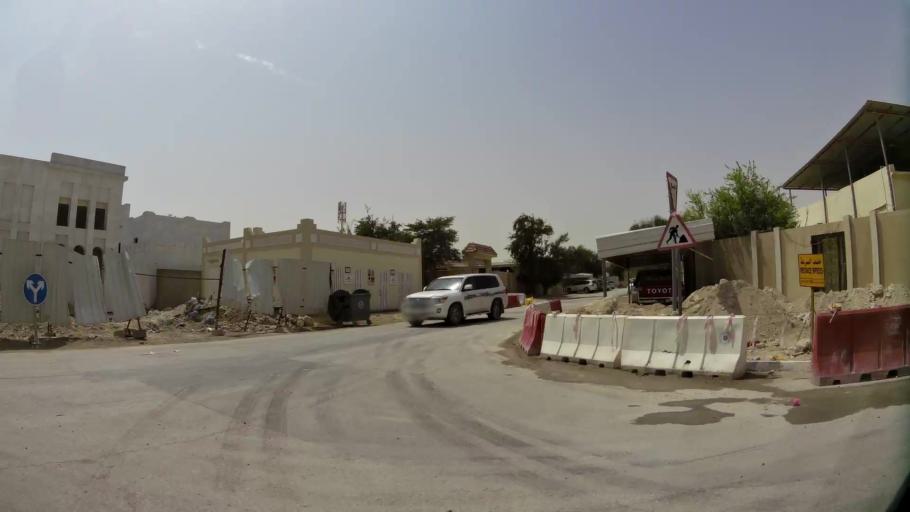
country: QA
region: Baladiyat ar Rayyan
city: Ar Rayyan
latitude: 25.2358
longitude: 51.4177
